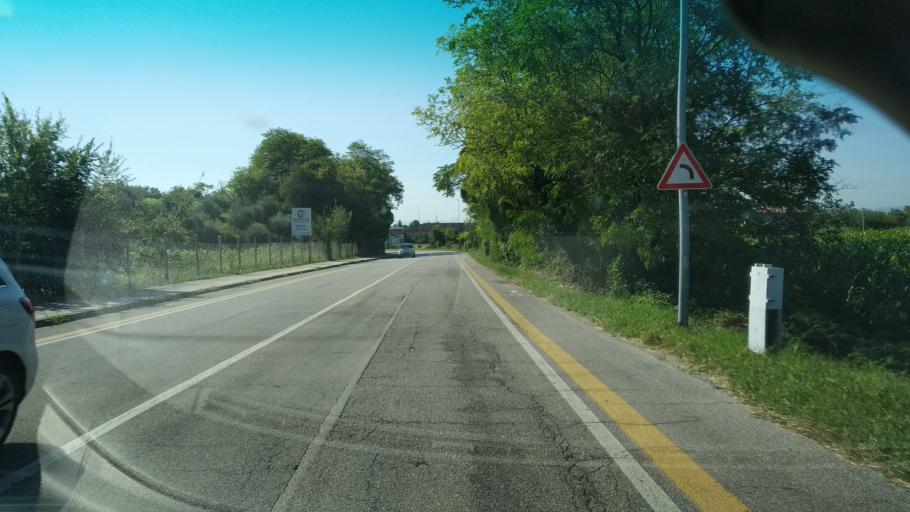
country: IT
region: Veneto
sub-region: Provincia di Vicenza
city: Bassano del Grappa
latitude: 45.7663
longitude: 11.7134
